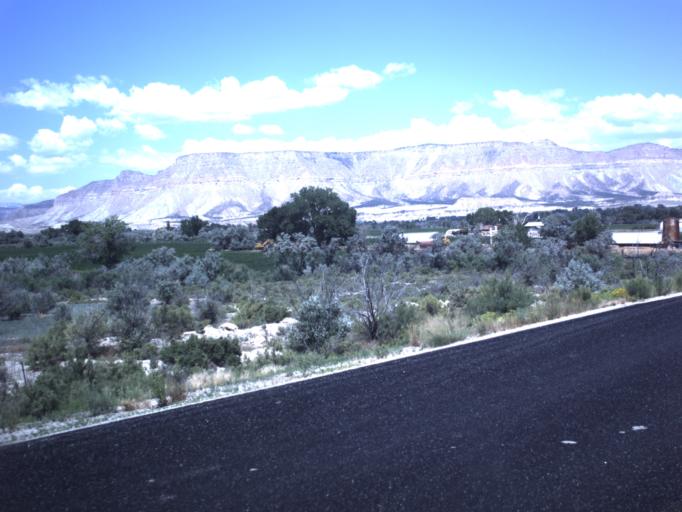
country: US
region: Utah
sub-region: Emery County
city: Ferron
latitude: 39.0655
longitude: -111.1314
